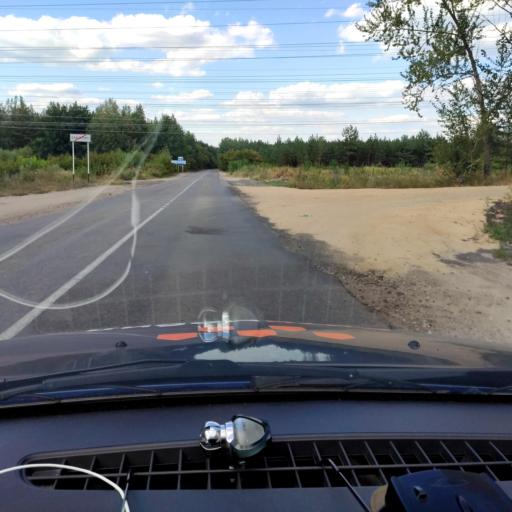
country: RU
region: Voronezj
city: Somovo
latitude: 51.7107
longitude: 39.3679
